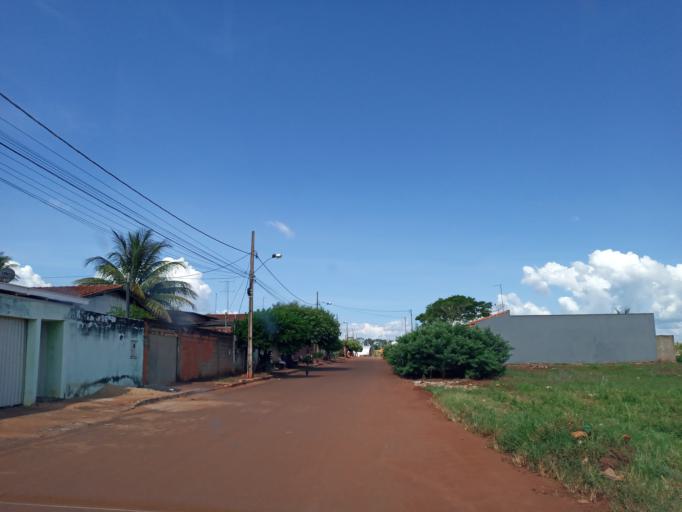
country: BR
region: Goias
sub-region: Itumbiara
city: Itumbiara
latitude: -18.4338
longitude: -49.1843
